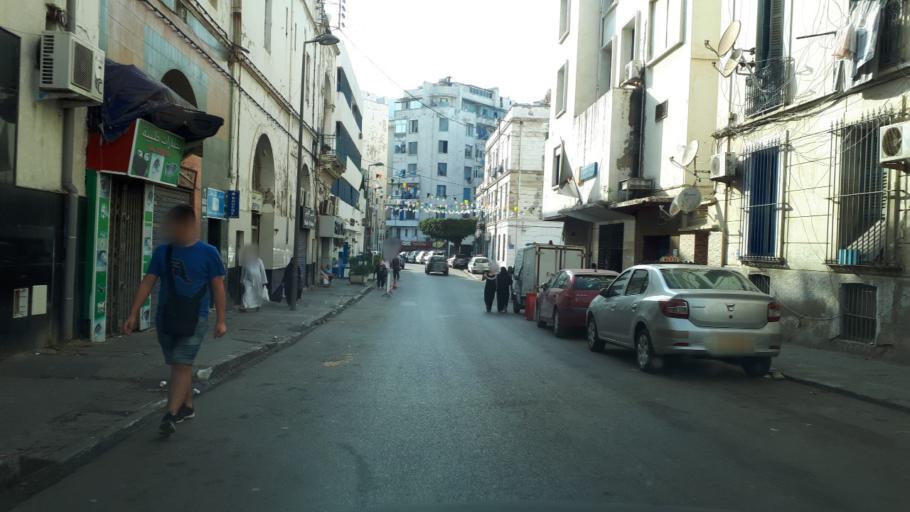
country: DZ
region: Alger
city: Algiers
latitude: 36.7916
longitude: 3.0538
